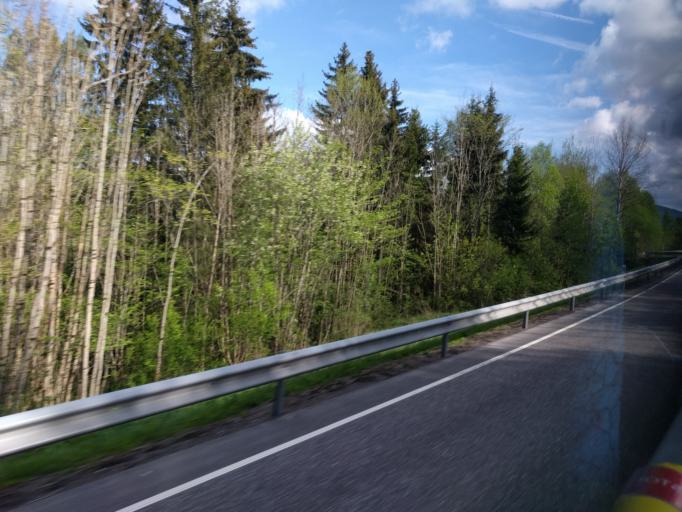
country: NO
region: Vestfold
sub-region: Lardal
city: Svarstad
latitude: 59.3611
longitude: 9.9154
